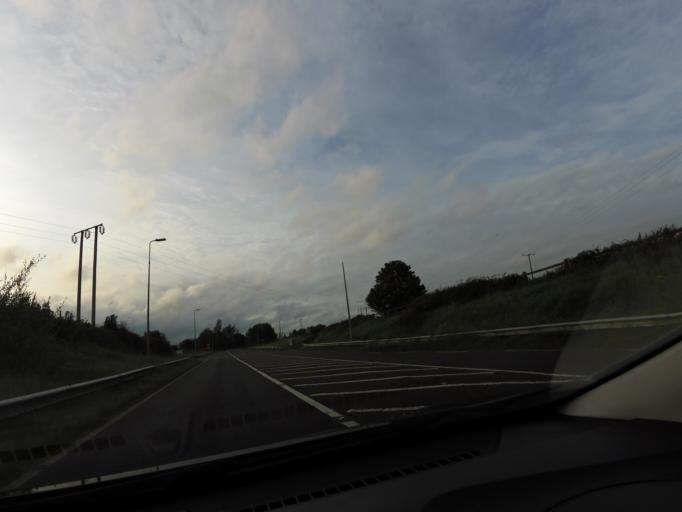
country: IE
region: Leinster
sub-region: Uibh Fhaili
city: Ferbane
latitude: 53.3033
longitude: -7.8205
